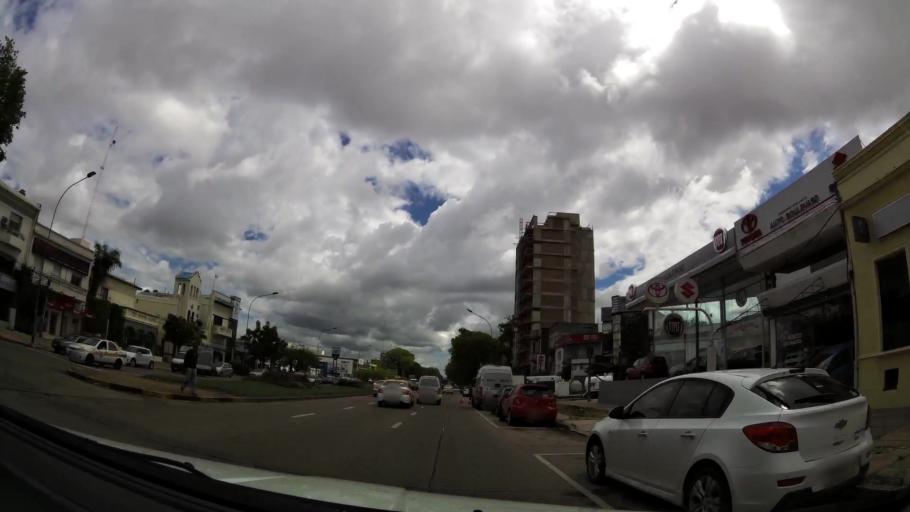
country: UY
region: Montevideo
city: Montevideo
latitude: -34.8906
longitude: -56.1653
